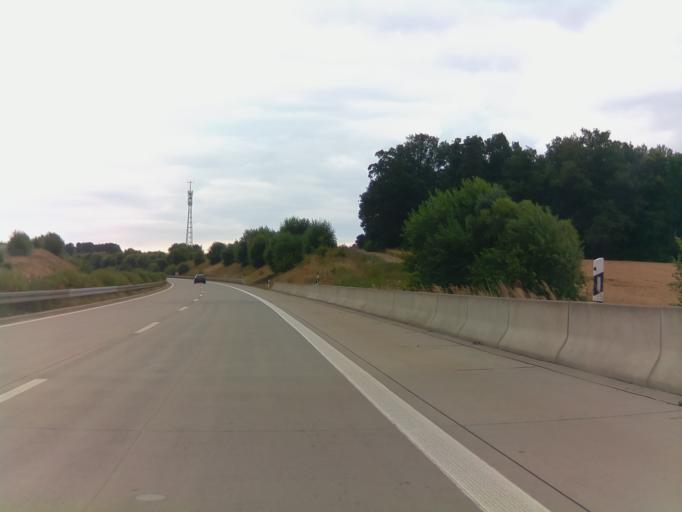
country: DE
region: Thuringia
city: Wolfershausen
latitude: 50.4928
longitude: 10.4411
